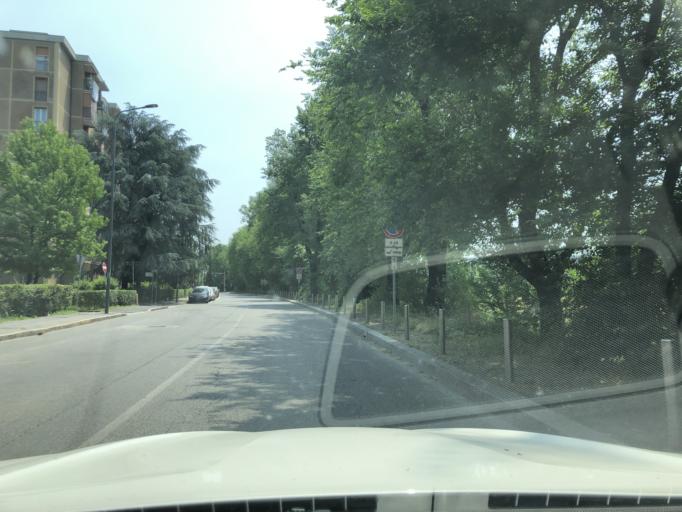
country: IT
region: Lombardy
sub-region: Citta metropolitana di Milano
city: Pero
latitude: 45.4973
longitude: 9.1004
